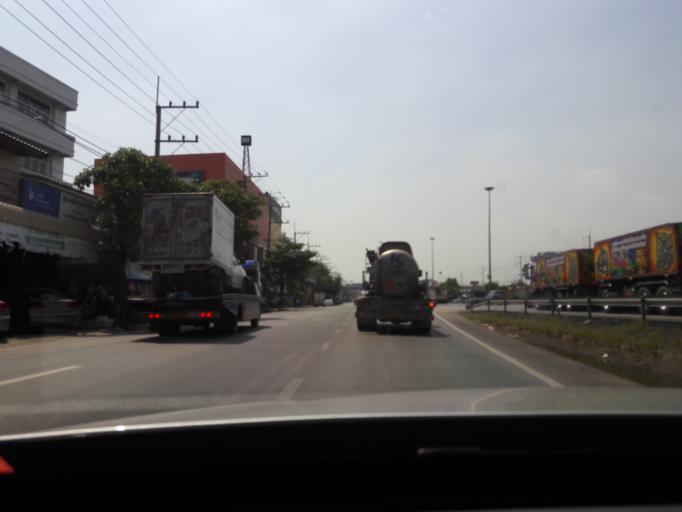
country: TH
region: Samut Sakhon
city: Samut Sakhon
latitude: 13.5515
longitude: 100.2652
